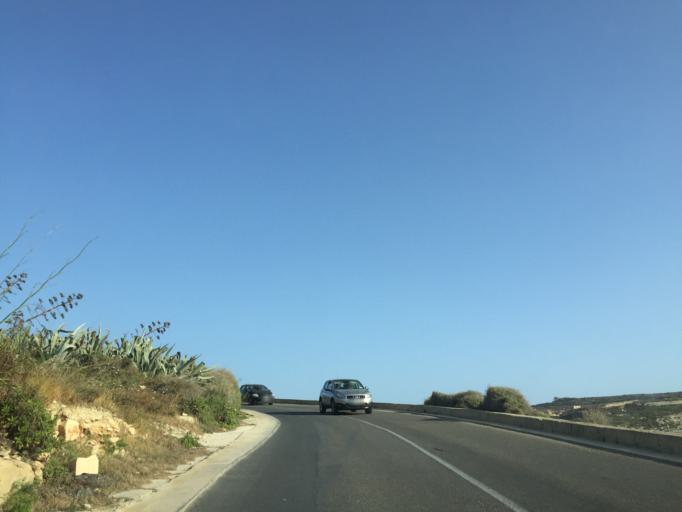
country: MT
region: Saint Lawrence
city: San Lawrenz
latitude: 36.0503
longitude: 14.1949
